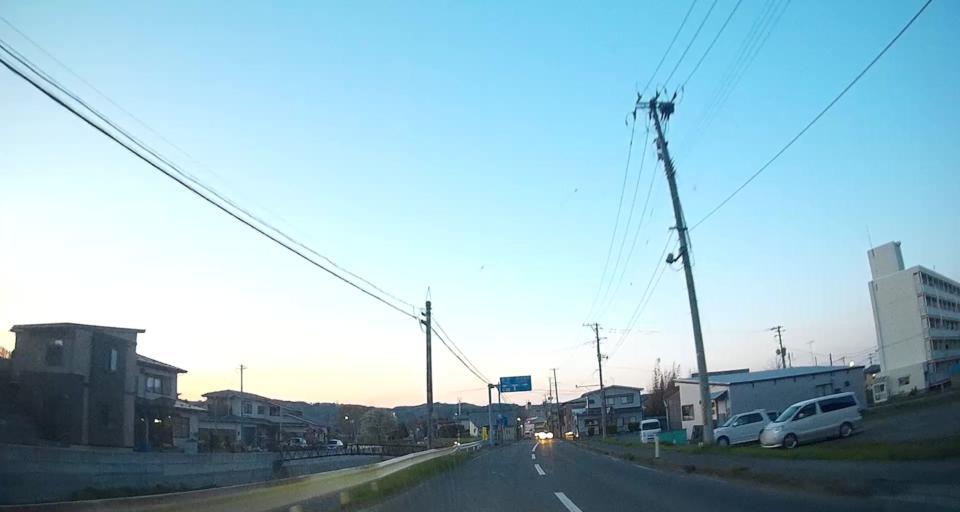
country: JP
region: Aomori
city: Hachinohe
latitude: 40.1843
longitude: 141.7718
